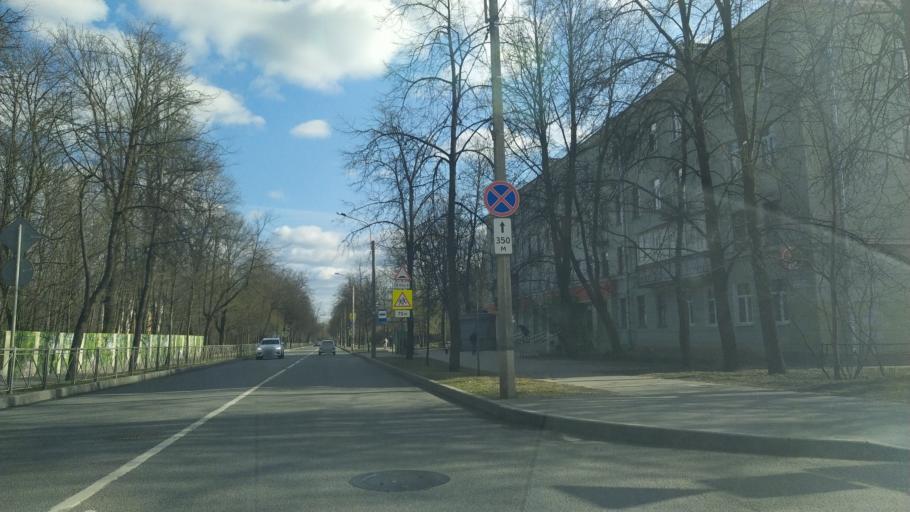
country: RU
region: St.-Petersburg
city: Pushkin
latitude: 59.7077
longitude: 30.4155
